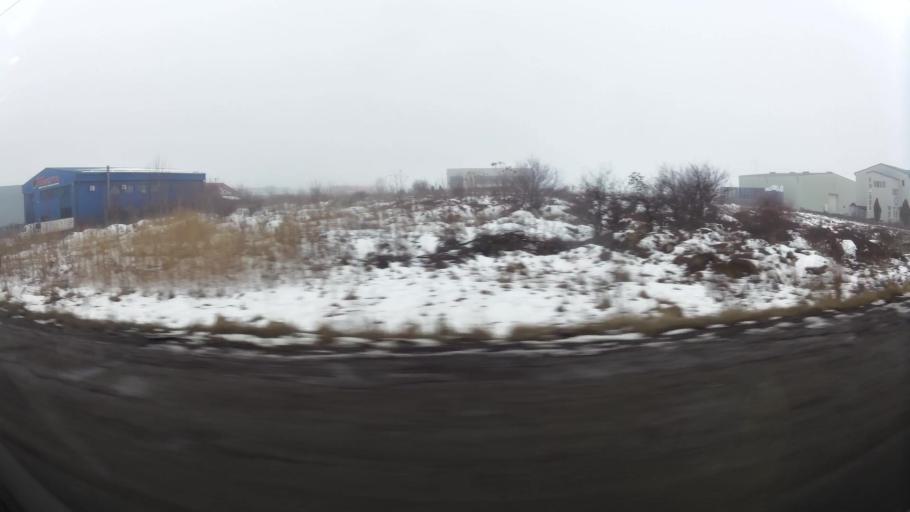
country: RO
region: Ilfov
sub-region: Comuna Clinceni
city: Olteni
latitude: 44.4097
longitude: 25.9742
